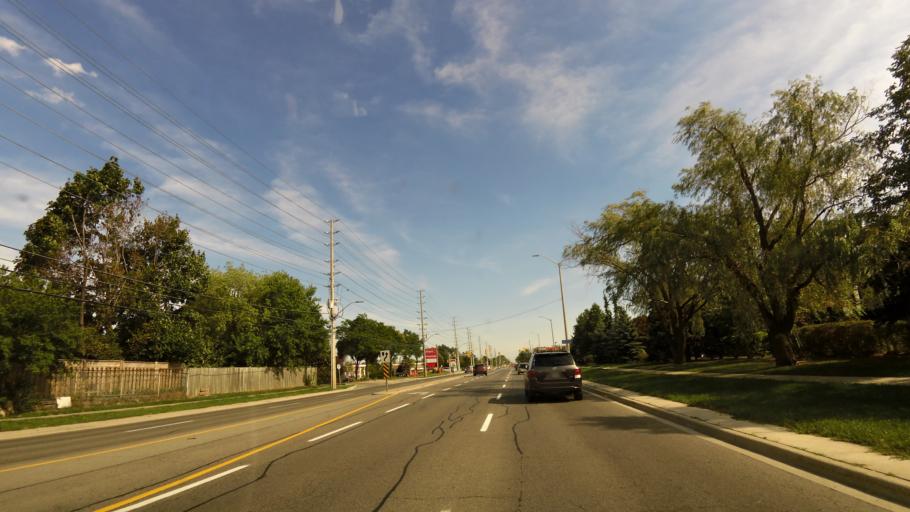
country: CA
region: Ontario
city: Mississauga
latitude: 43.5265
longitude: -79.6868
